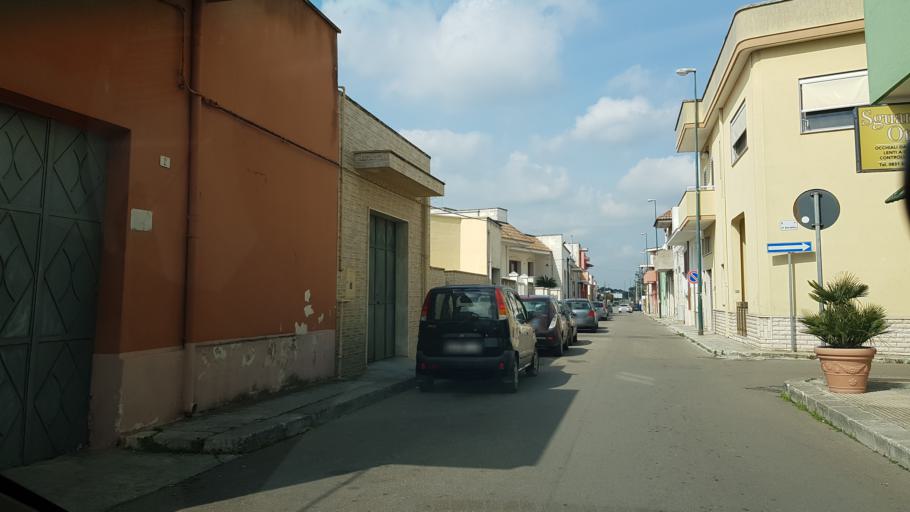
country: IT
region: Apulia
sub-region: Provincia di Brindisi
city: Torchiarolo
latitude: 40.4866
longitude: 18.0509
